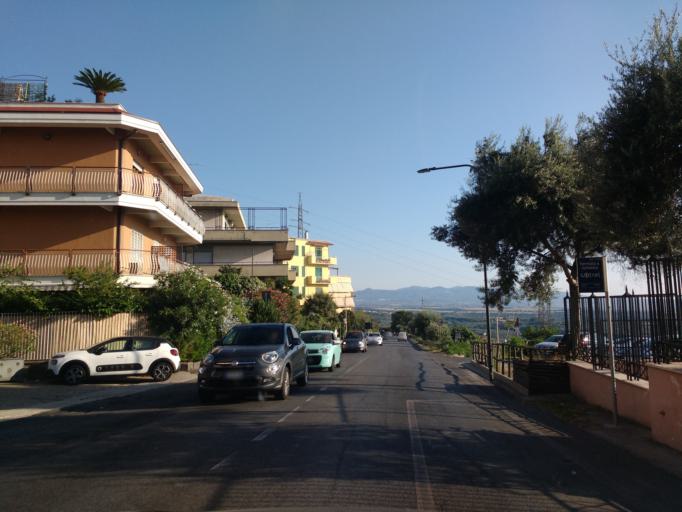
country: IT
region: Latium
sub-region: Citta metropolitana di Roma Capitale
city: Tivoli
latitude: 41.9537
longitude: 12.7914
